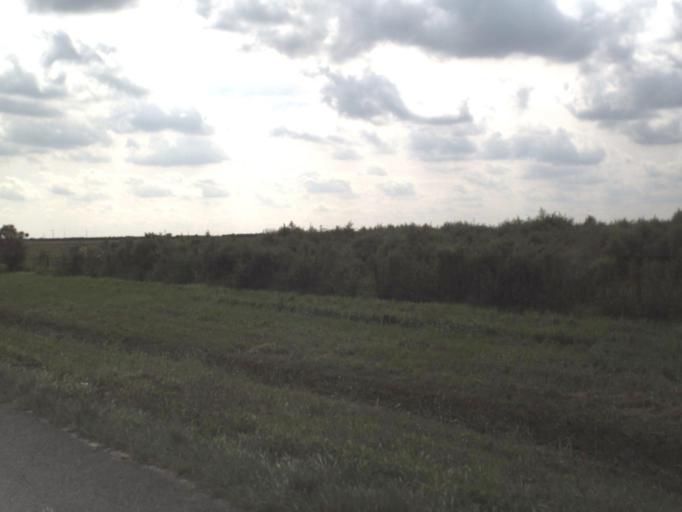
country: US
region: Florida
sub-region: Okeechobee County
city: Cypress Quarters
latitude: 27.4412
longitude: -80.8111
